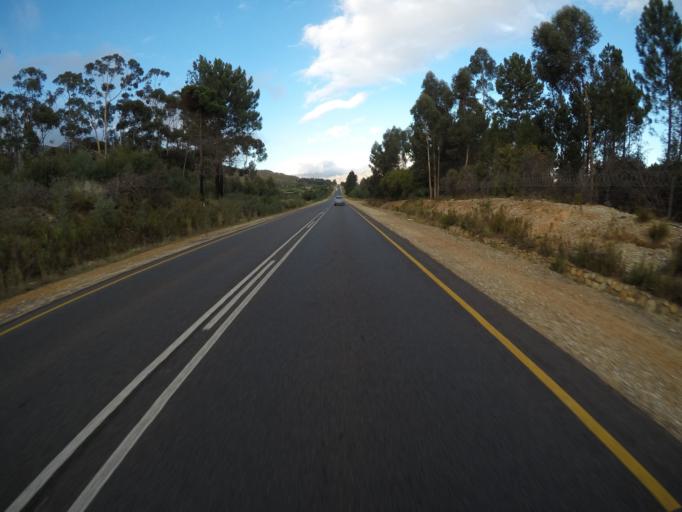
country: ZA
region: Western Cape
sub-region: Overberg District Municipality
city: Grabouw
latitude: -34.0219
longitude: 19.2247
